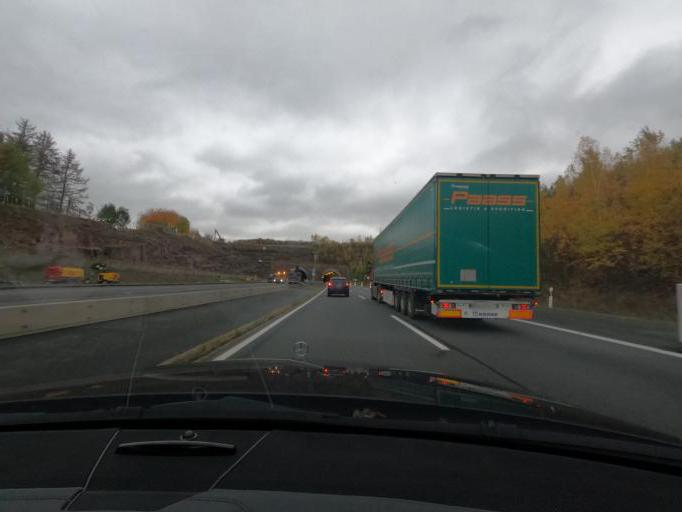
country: DE
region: Thuringia
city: Rustenfelde
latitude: 51.3991
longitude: 9.9804
